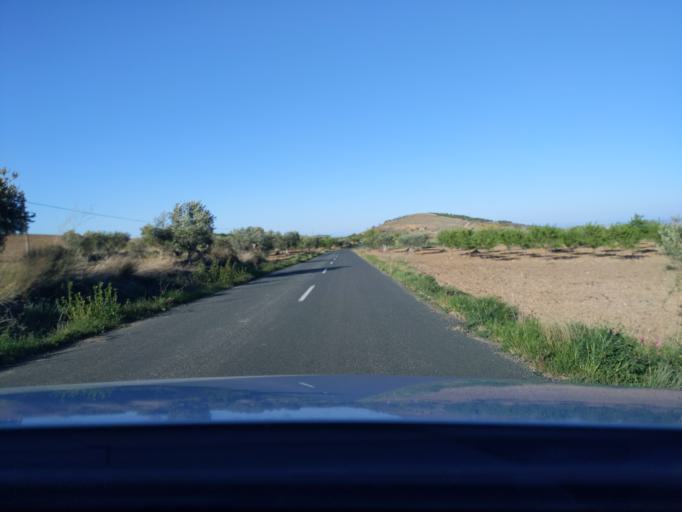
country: ES
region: La Rioja
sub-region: Provincia de La Rioja
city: Bergasa
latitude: 42.2666
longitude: -2.1033
